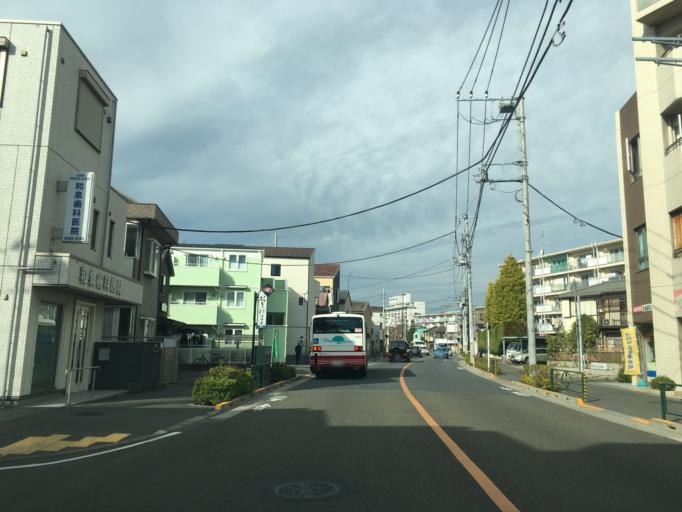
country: JP
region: Tokyo
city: Chofugaoka
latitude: 35.6411
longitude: 139.5693
